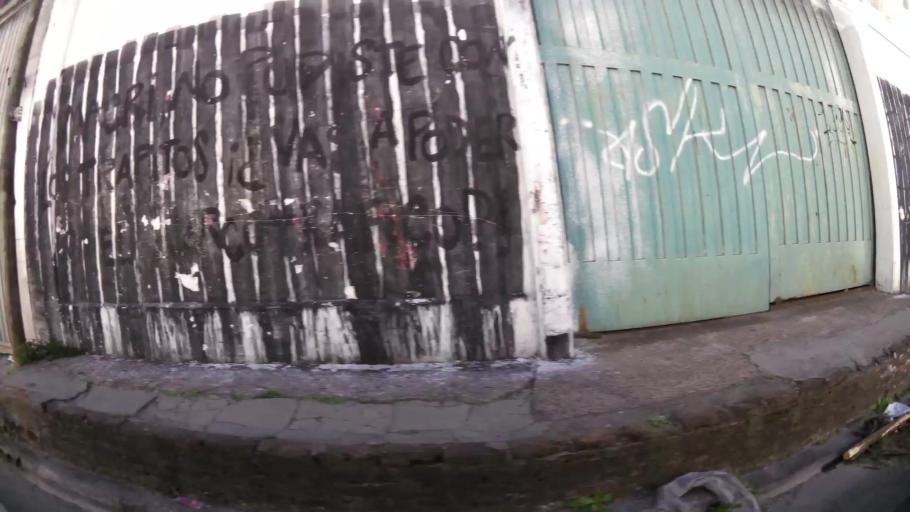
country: AR
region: Buenos Aires
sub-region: Partido de General San Martin
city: General San Martin
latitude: -34.5353
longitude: -58.5413
